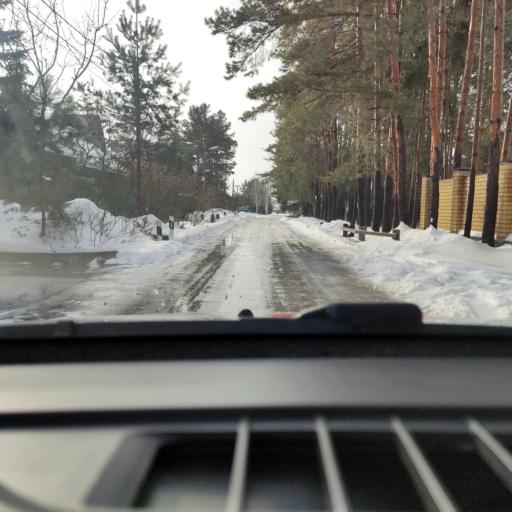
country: RU
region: Voronezj
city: Podgornoye
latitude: 51.7763
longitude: 39.1312
